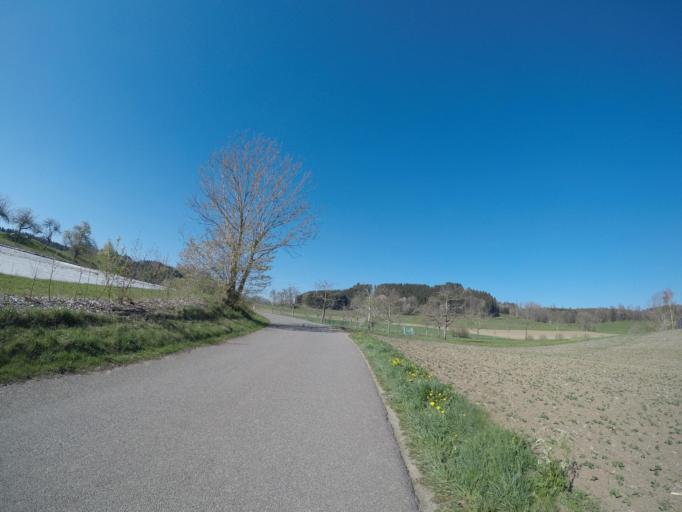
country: DE
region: Baden-Wuerttemberg
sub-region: Tuebingen Region
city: Ebenweiler
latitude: 47.8819
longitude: 9.5152
